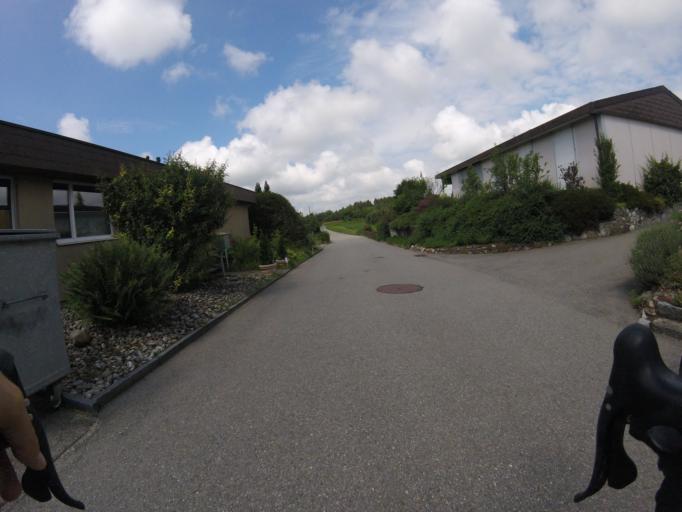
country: CH
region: Bern
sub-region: Bern-Mittelland District
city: Bariswil
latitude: 47.0176
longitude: 7.5223
